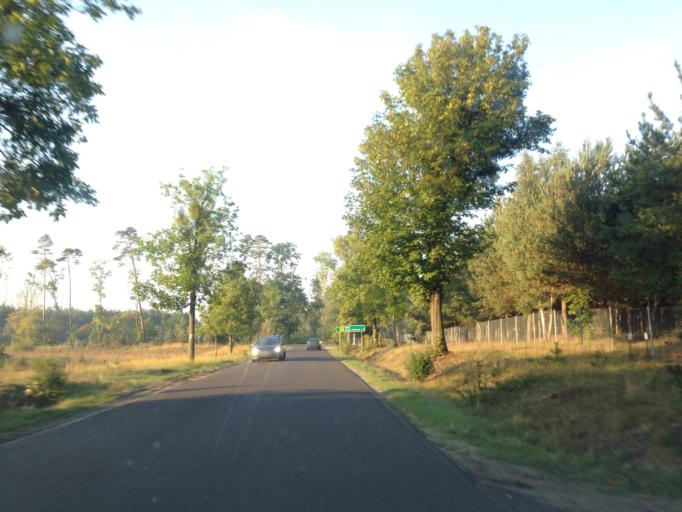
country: PL
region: Kujawsko-Pomorskie
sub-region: Powiat golubsko-dobrzynski
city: Radomin
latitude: 53.1051
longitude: 19.1287
